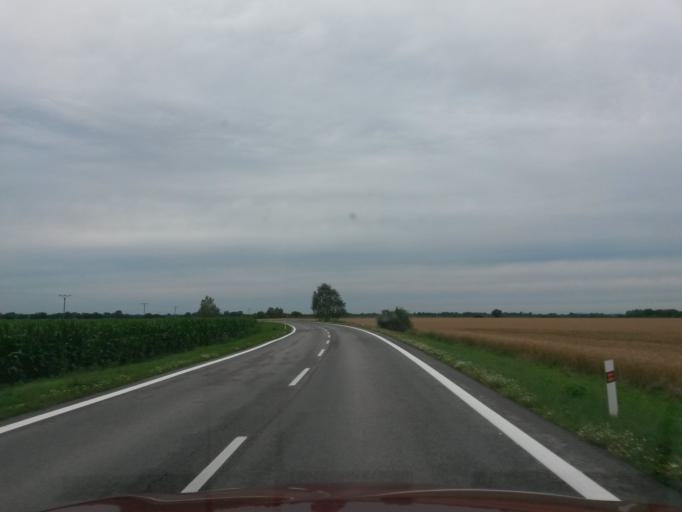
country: SK
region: Nitriansky
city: Zeliezovce
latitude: 48.1244
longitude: 18.6885
